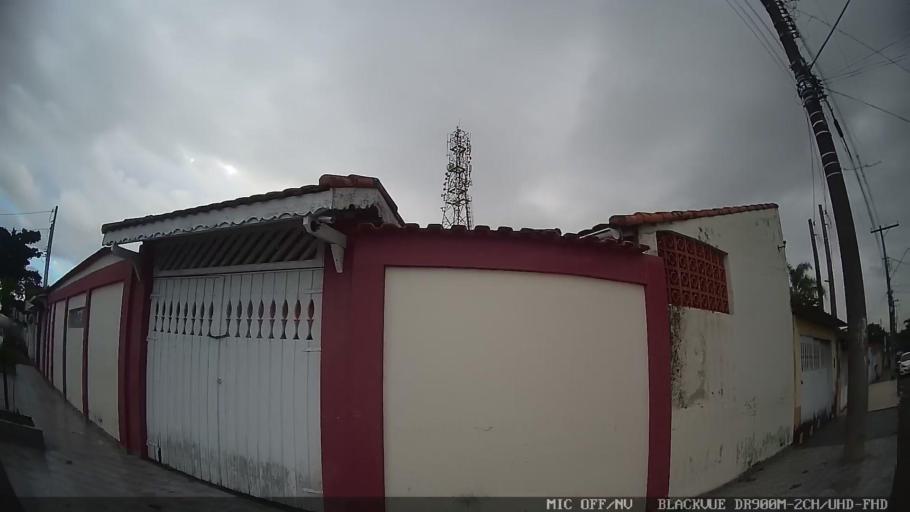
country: BR
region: Sao Paulo
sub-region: Itanhaem
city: Itanhaem
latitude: -24.1774
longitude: -46.7907
